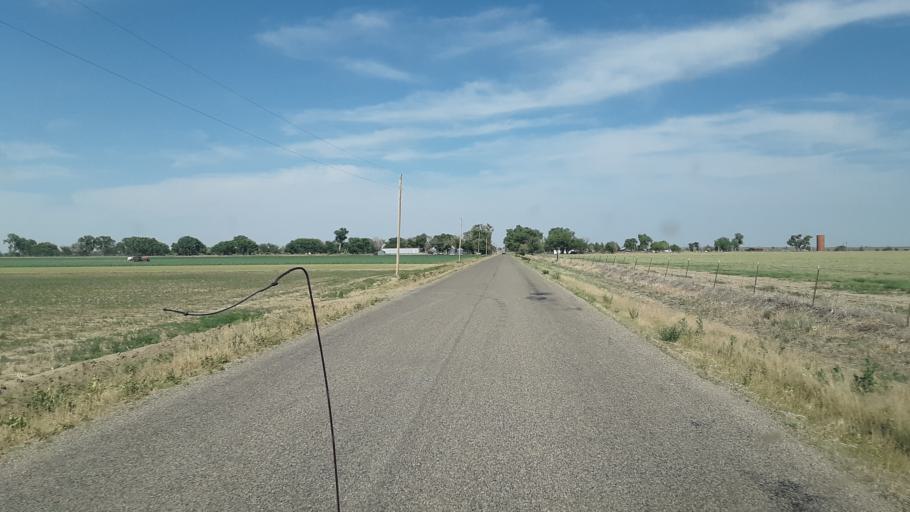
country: US
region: Colorado
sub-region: Otero County
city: Fowler
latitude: 38.1632
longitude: -103.9198
